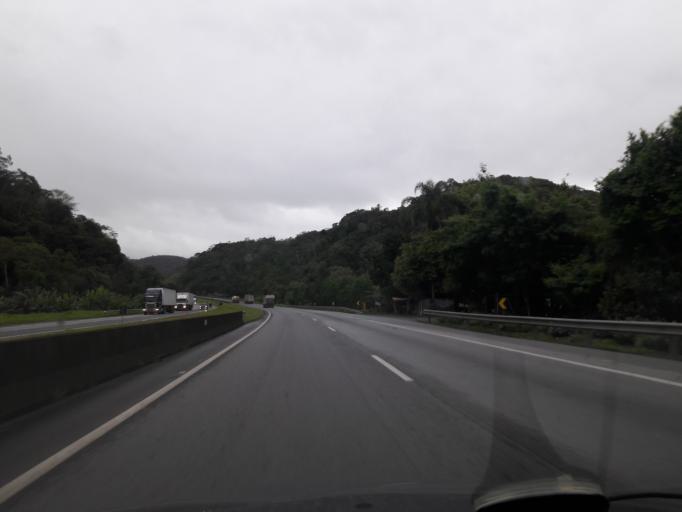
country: BR
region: Sao Paulo
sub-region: Miracatu
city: Miracatu
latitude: -24.2397
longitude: -47.3619
